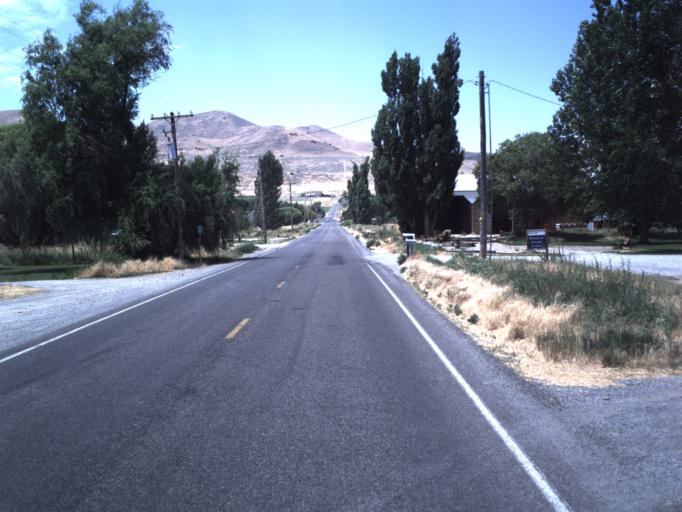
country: US
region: Utah
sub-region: Box Elder County
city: Tremonton
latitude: 41.6945
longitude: -112.2865
